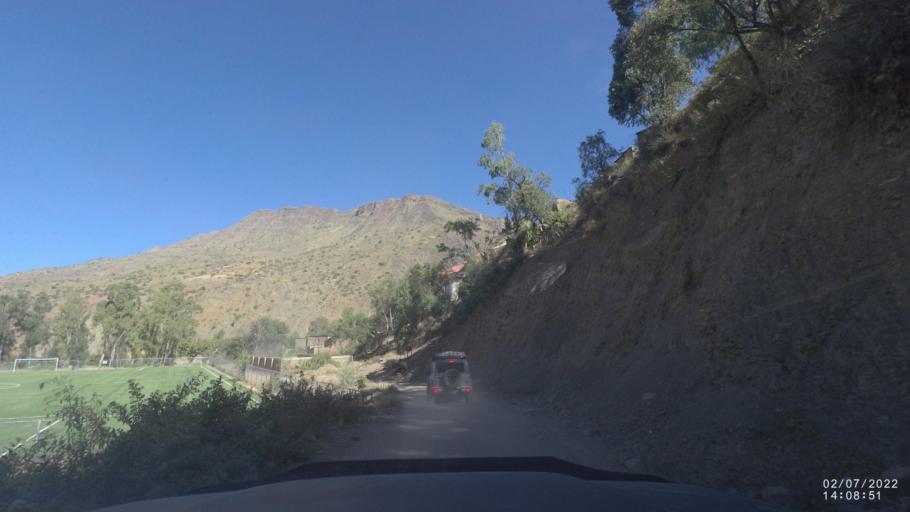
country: BO
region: Cochabamba
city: Irpa Irpa
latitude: -17.8202
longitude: -66.4027
